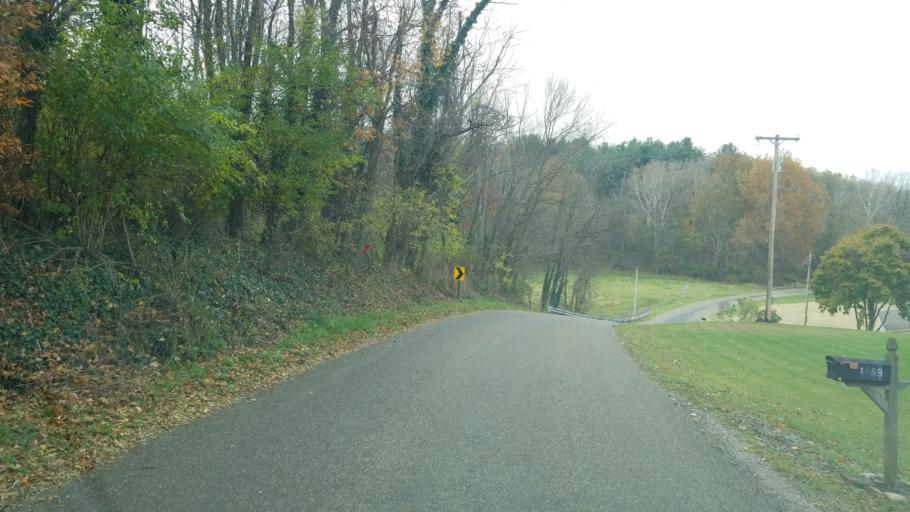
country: US
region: Ohio
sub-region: Richland County
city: Mansfield
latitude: 40.7167
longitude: -82.4956
